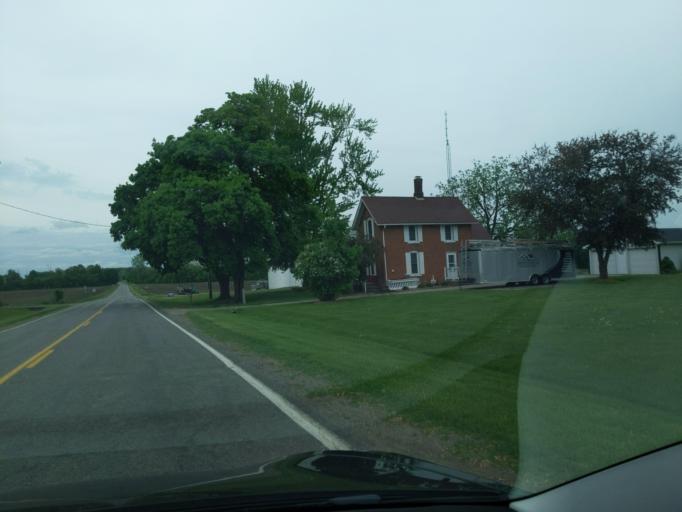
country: US
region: Michigan
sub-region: Ingham County
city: Mason
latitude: 42.5461
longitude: -84.4233
